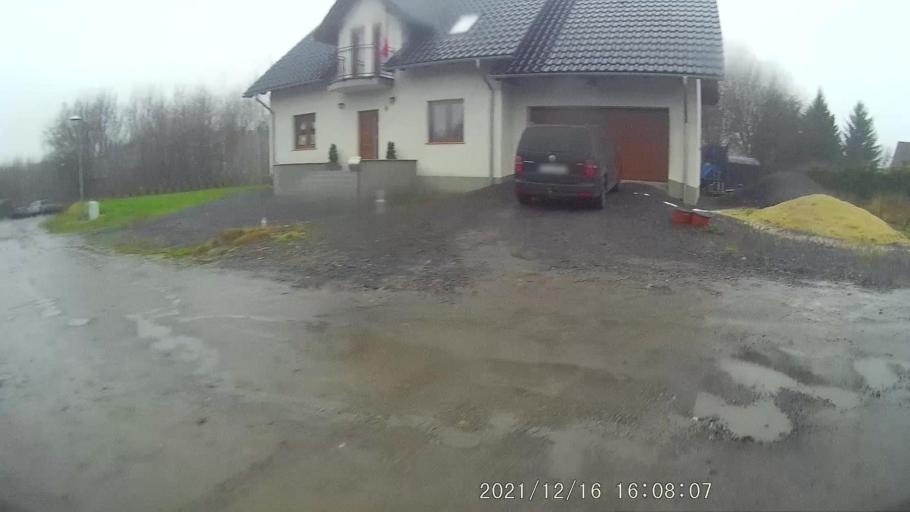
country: PL
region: Lower Silesian Voivodeship
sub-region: Powiat zgorzelecki
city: Lagow
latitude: 51.1581
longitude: 15.0499
